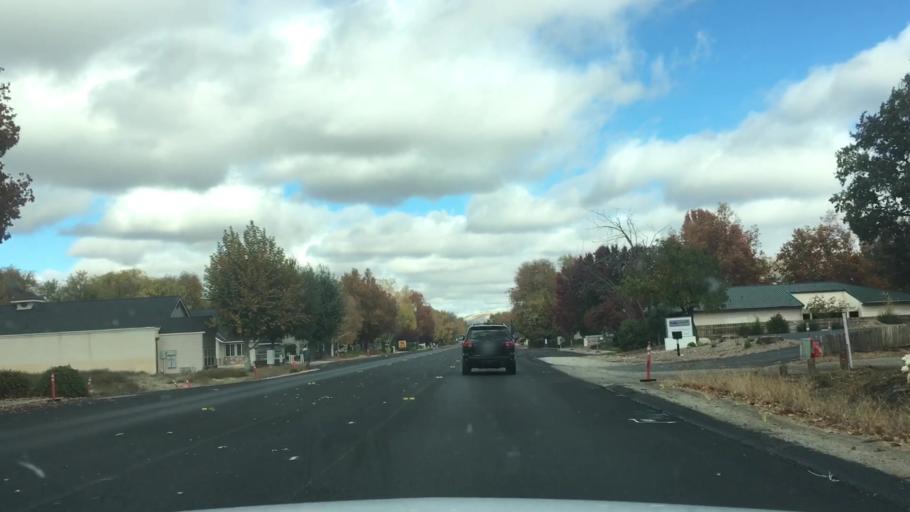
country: US
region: California
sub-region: San Luis Obispo County
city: Atascadero
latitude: 35.4756
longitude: -120.6679
